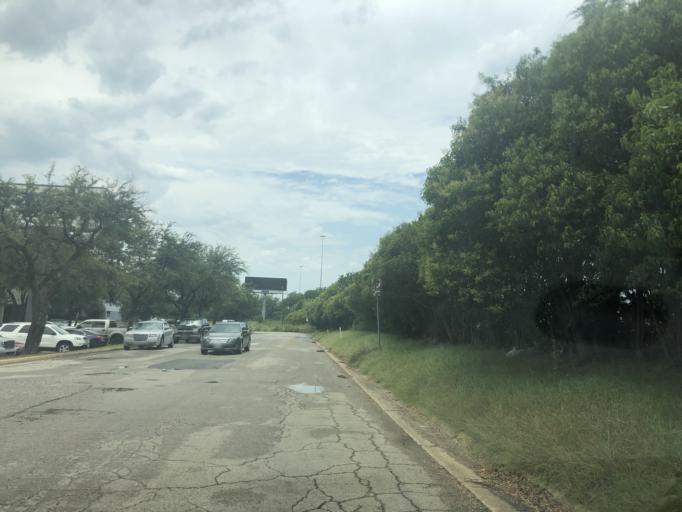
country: US
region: Texas
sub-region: Dallas County
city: Grand Prairie
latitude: 32.7590
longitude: -97.0426
